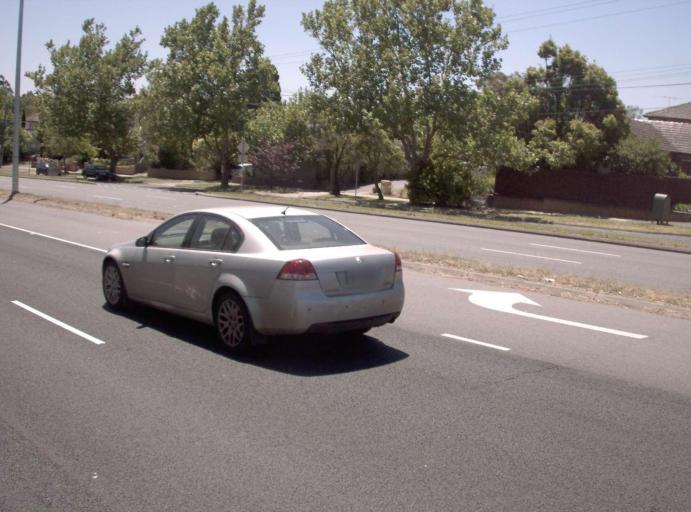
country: AU
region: Victoria
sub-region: Glen Eira
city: Murrumbeena
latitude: -37.8864
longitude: 145.0758
